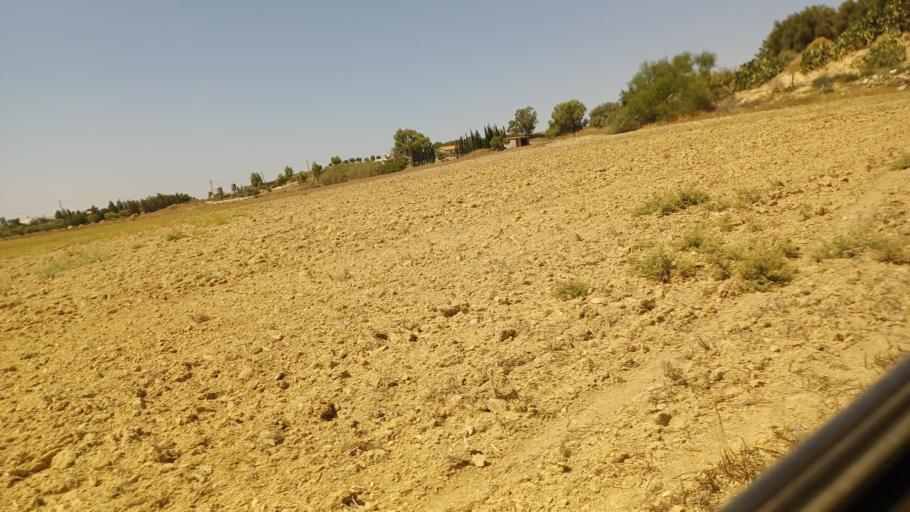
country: CY
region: Ammochostos
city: Acheritou
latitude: 35.0880
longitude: 33.8745
